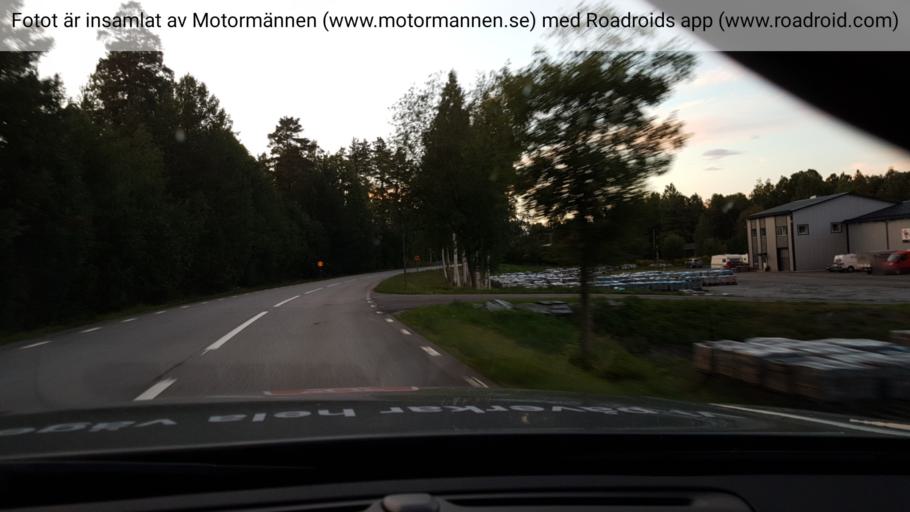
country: SE
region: OErebro
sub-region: Hallefors Kommun
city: Haellefors
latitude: 59.7002
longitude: 14.5290
